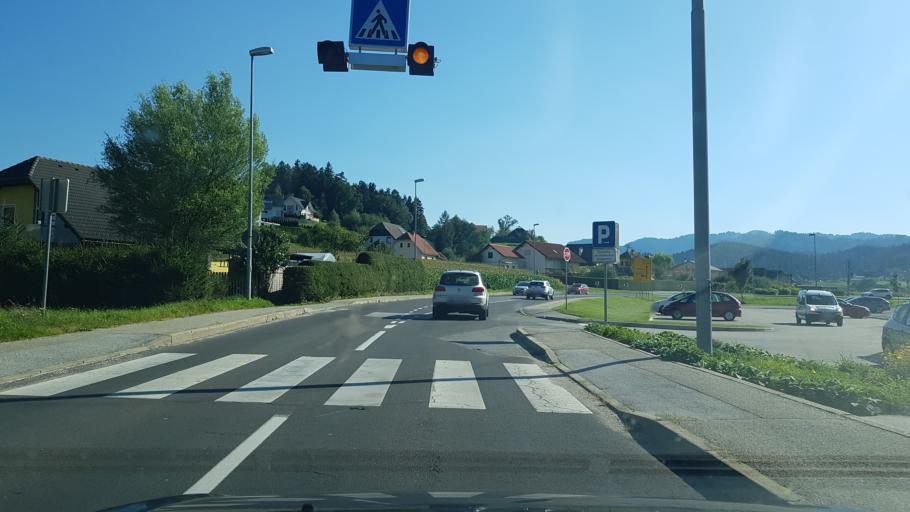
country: SI
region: Slovenj Gradec
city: Slovenj Gradec
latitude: 46.5012
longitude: 15.0739
